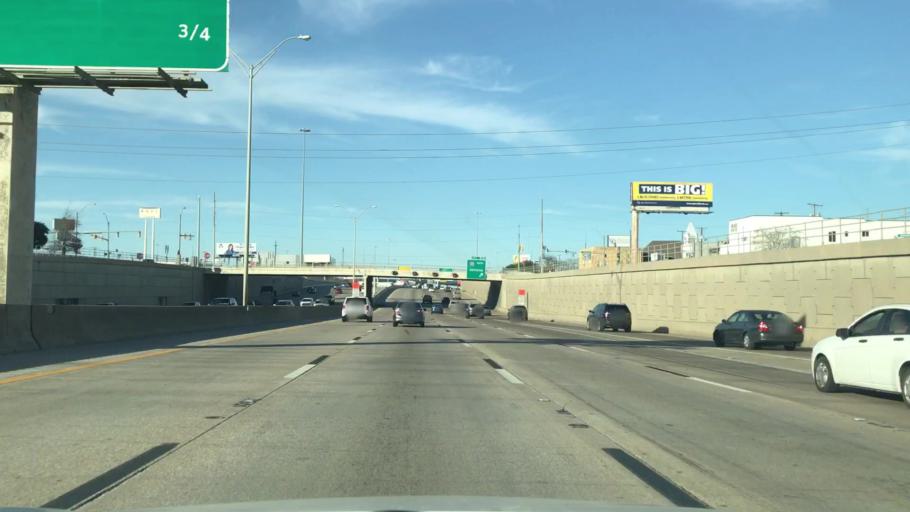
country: US
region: Texas
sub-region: Tarrant County
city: Fort Worth
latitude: 32.7361
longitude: -97.3204
